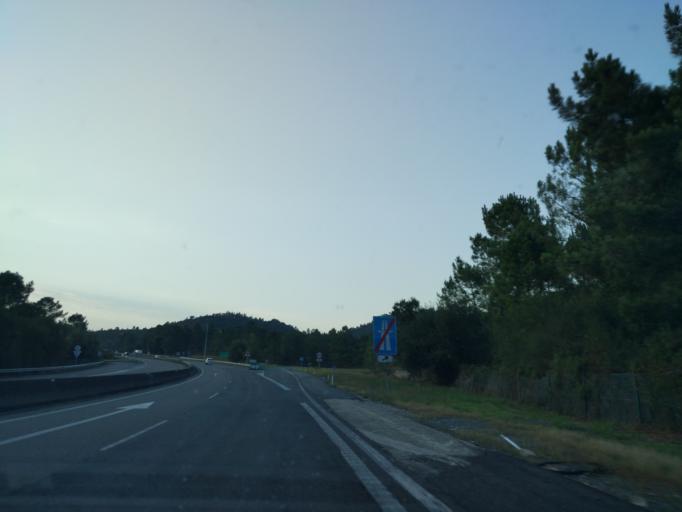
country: ES
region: Galicia
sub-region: Provincia da Coruna
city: Padron
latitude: 42.7317
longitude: -8.6363
